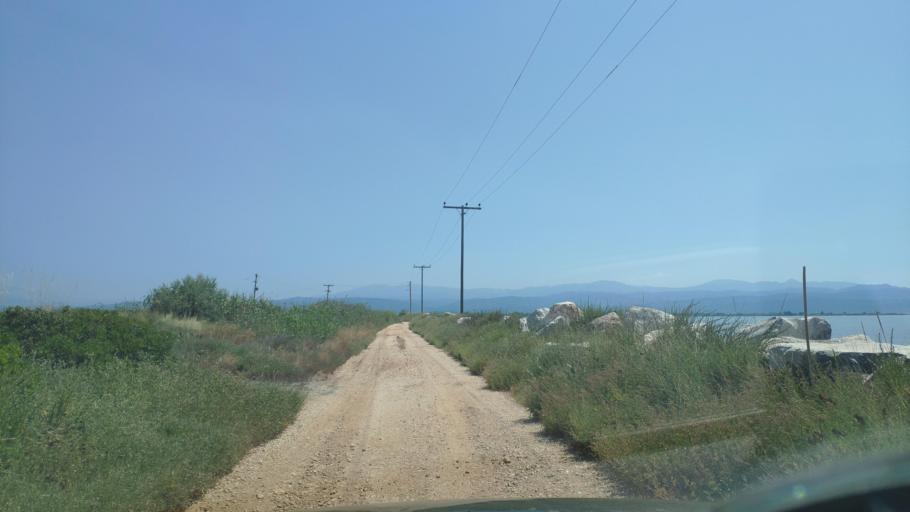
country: GR
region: Epirus
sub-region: Nomos Artas
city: Aneza
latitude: 39.0250
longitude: 20.9389
